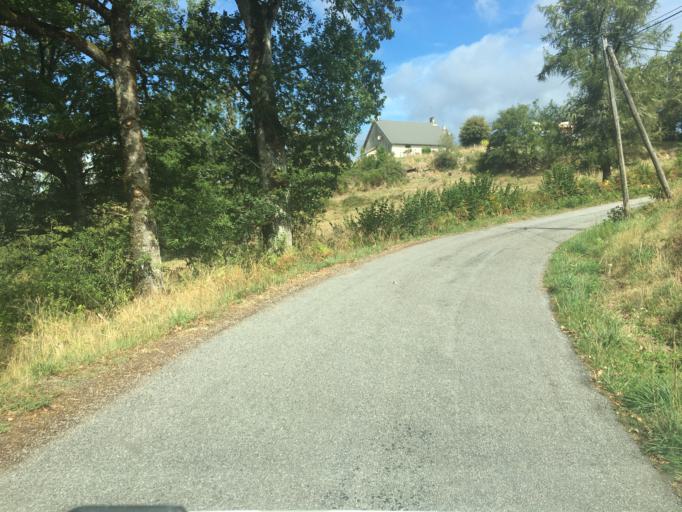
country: FR
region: Auvergne
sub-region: Departement du Cantal
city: Champagnac
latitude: 45.4253
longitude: 2.4081
